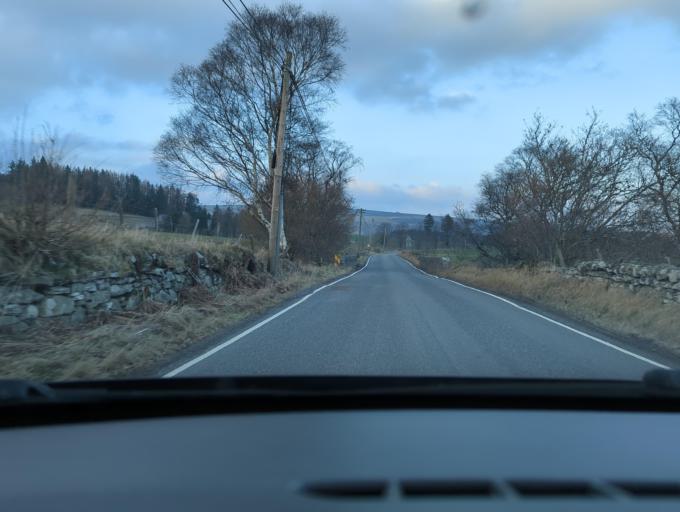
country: GB
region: Scotland
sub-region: Perth and Kinross
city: Aberfeldy
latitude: 56.5291
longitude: -3.7212
